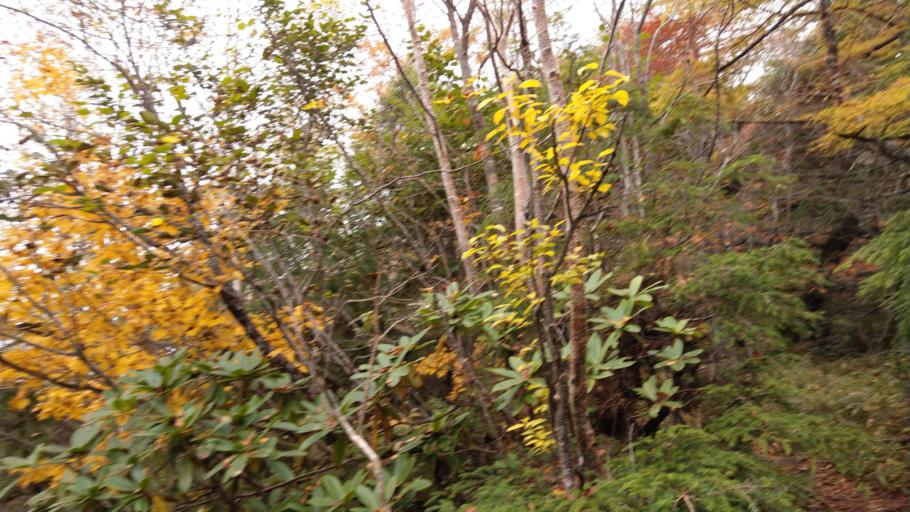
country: JP
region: Nagano
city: Komoro
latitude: 36.4034
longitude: 138.4586
